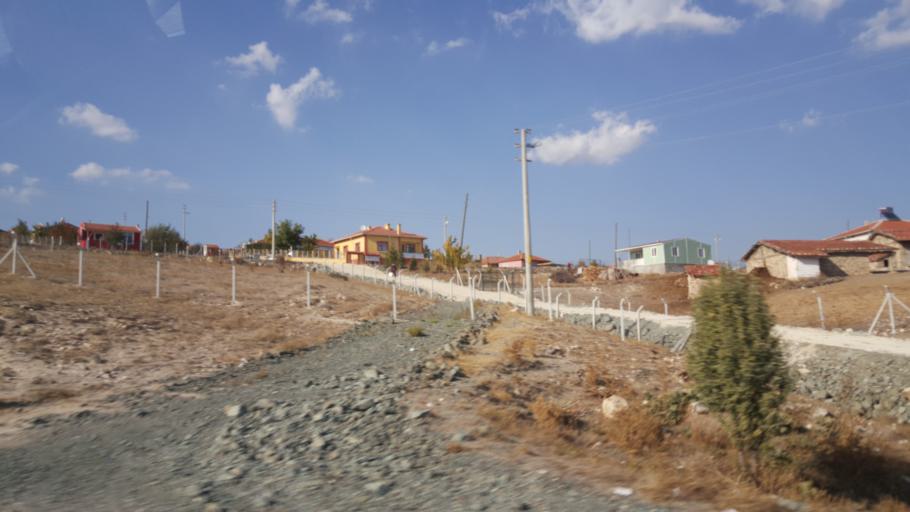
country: TR
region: Eskisehir
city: Kirka
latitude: 39.3246
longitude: 30.5633
